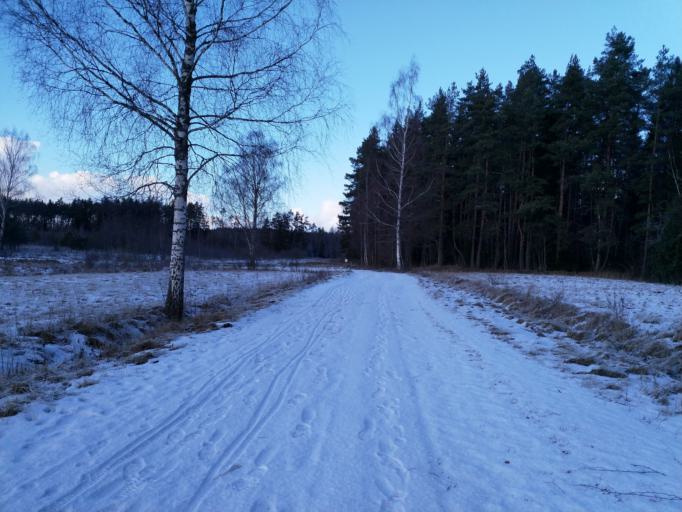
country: LV
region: Skrunda
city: Skrunda
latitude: 56.6756
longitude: 22.0833
